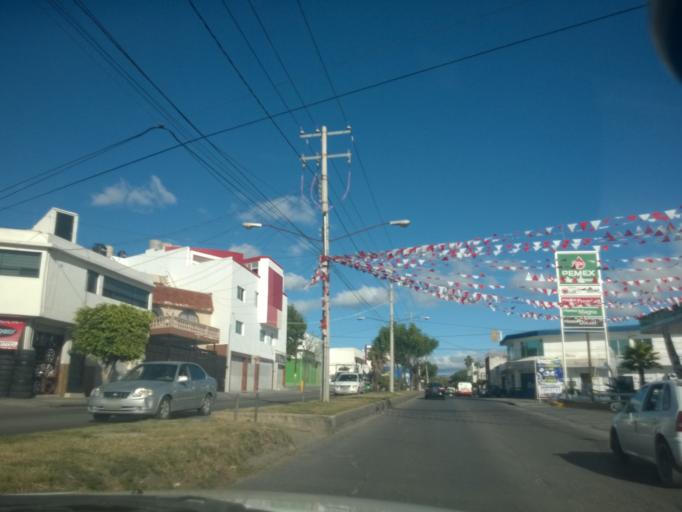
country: MX
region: Guanajuato
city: Leon
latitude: 21.1158
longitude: -101.6957
